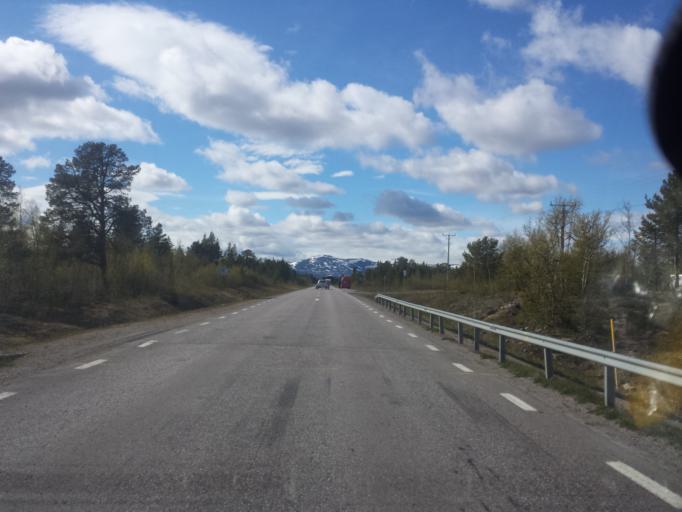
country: SE
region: Norrbotten
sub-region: Kiruna Kommun
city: Kiruna
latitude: 67.9906
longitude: 19.9239
